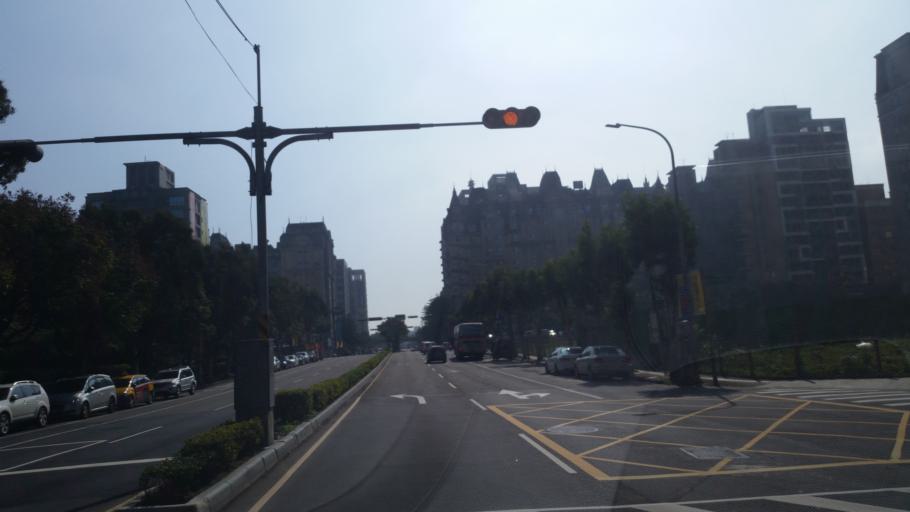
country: TW
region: Taiwan
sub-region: Taoyuan
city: Taoyuan
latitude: 25.0728
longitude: 121.3677
